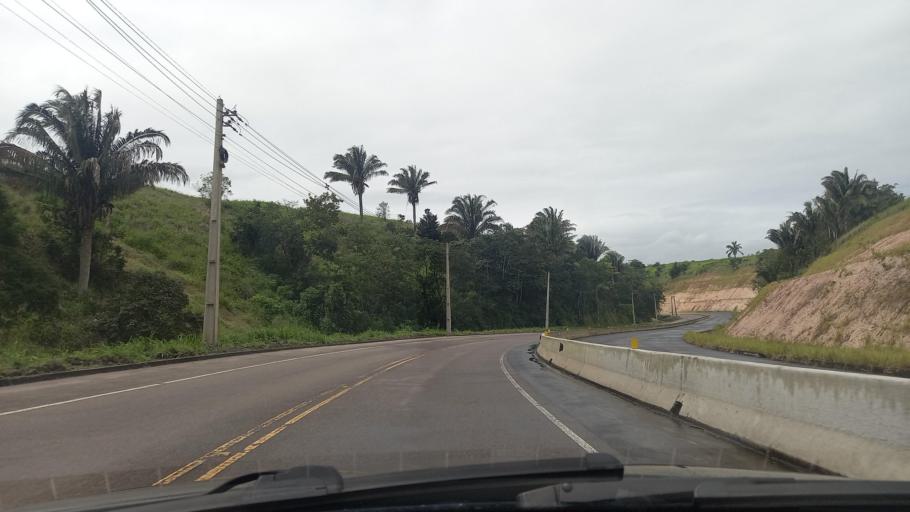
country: BR
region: Alagoas
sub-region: Campo Alegre
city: Campo Alegre
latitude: -9.8217
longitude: -36.2286
